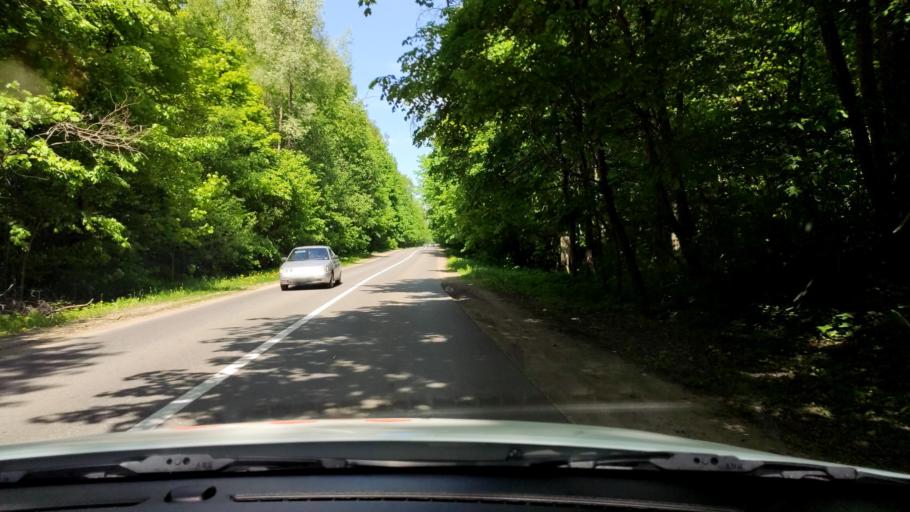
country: RU
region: Tatarstan
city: Osinovo
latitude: 55.8420
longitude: 48.8174
